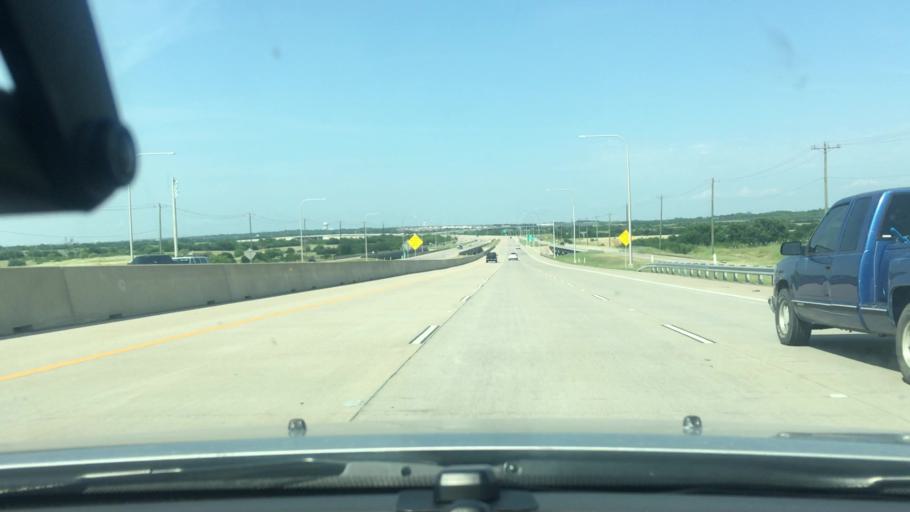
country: US
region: Texas
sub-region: Collin County
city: Frisco
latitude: 33.1976
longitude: -96.8327
